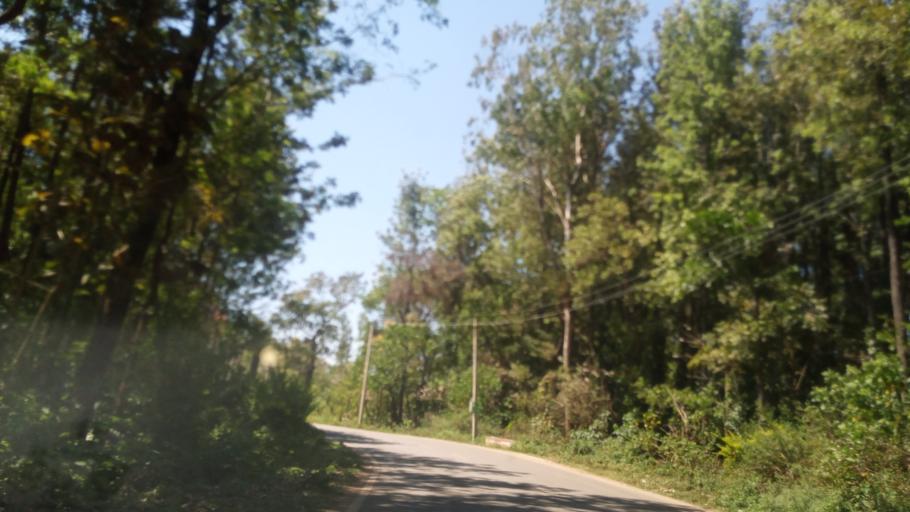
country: IN
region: Karnataka
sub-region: Chikmagalur
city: Chikmagalur
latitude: 13.4236
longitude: 75.8038
